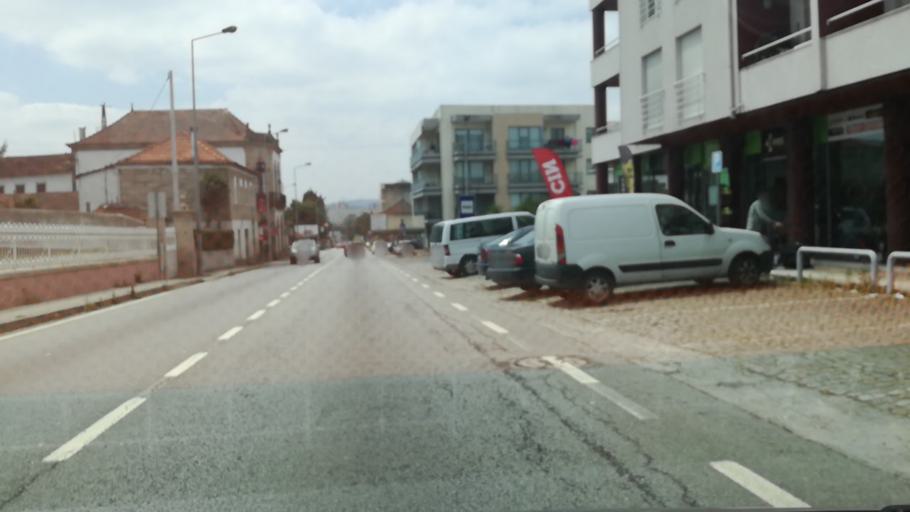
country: PT
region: Braga
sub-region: Vila Nova de Famalicao
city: Ferreiros
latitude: 41.3507
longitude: -8.5548
